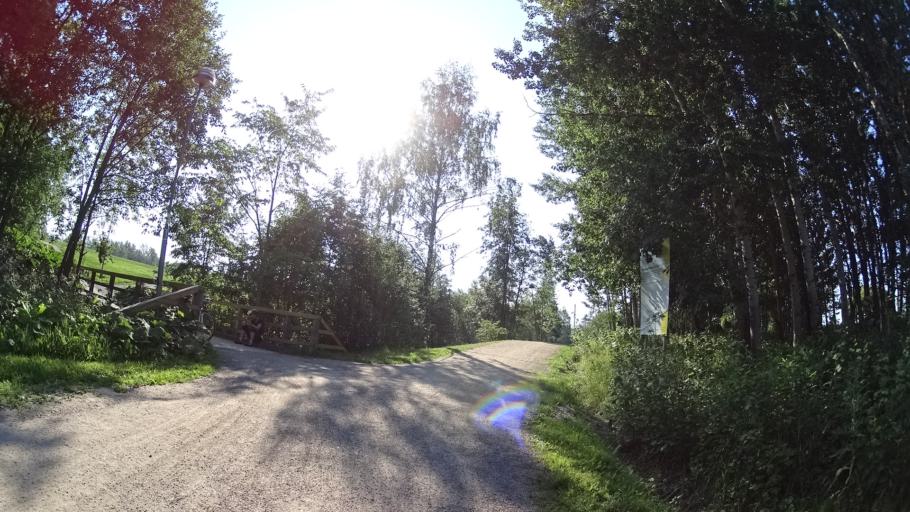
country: FI
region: Uusimaa
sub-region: Helsinki
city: Vantaa
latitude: 60.2759
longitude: 24.9818
